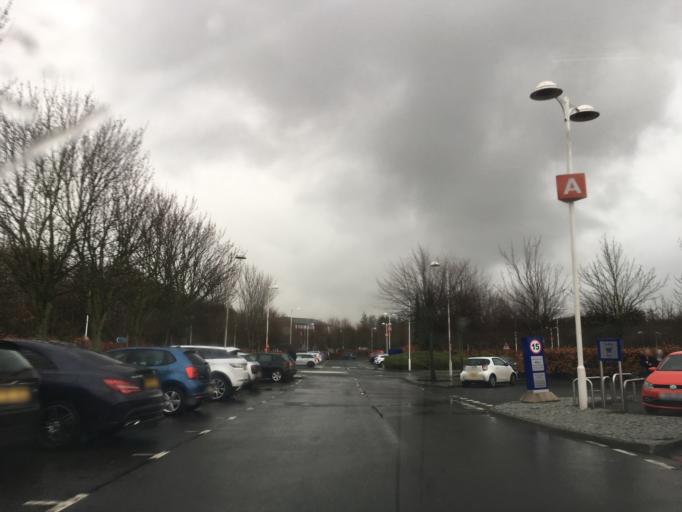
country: GB
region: Scotland
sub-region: Edinburgh
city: Currie
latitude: 55.9376
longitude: -3.3098
